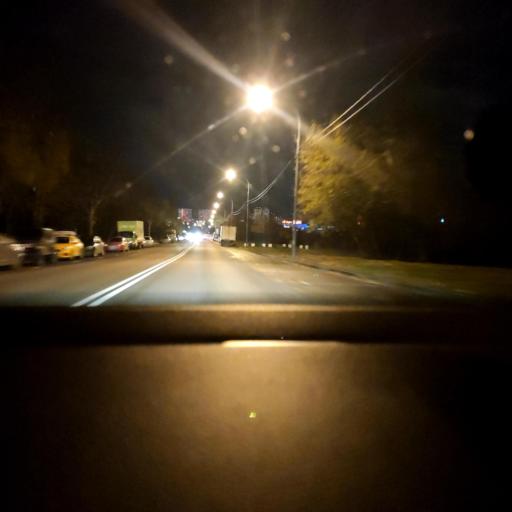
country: RU
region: Moscow
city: Orekhovo-Borisovo
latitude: 55.5981
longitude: 37.7147
